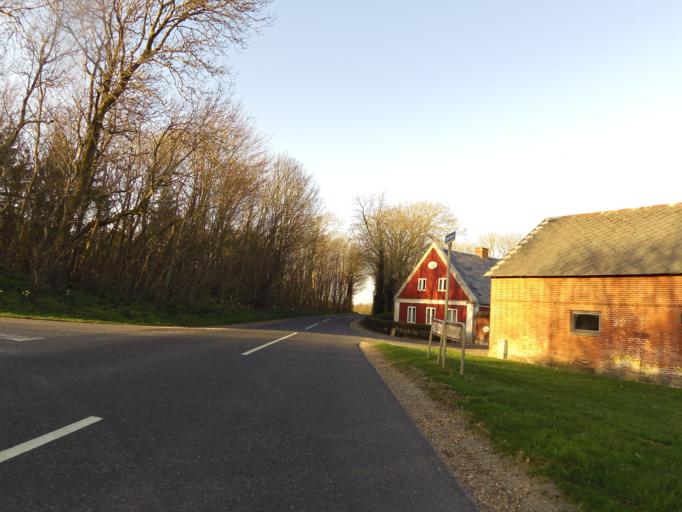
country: DK
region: Central Jutland
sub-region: Holstebro Kommune
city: Vinderup
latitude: 56.5179
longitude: 8.7745
